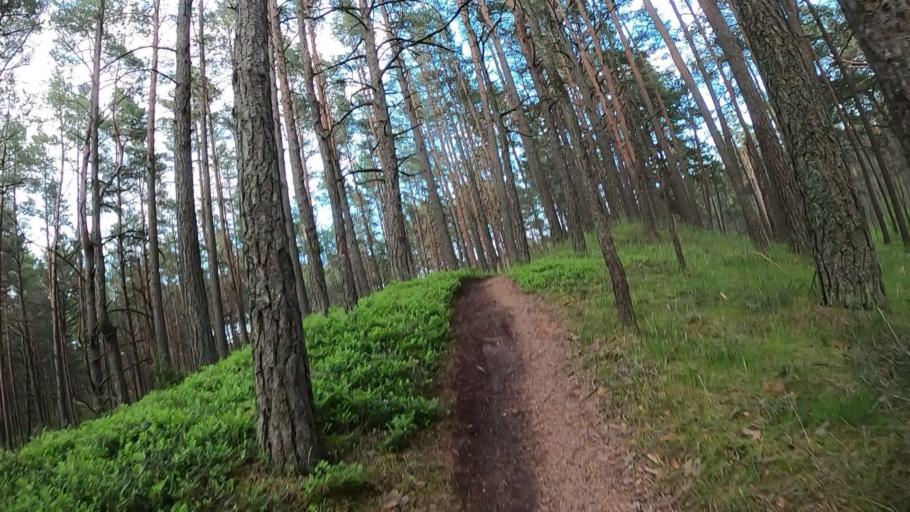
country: LV
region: Carnikava
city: Carnikava
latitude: 57.1261
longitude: 24.2180
